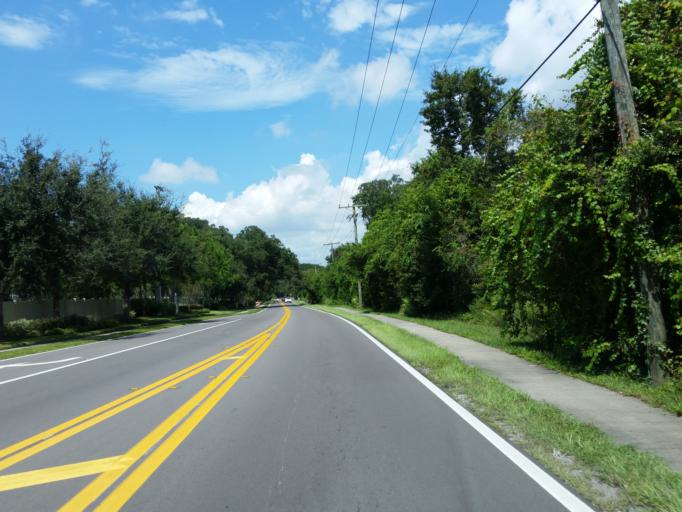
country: US
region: Florida
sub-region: Hillsborough County
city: Riverview
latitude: 27.8401
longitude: -82.3111
